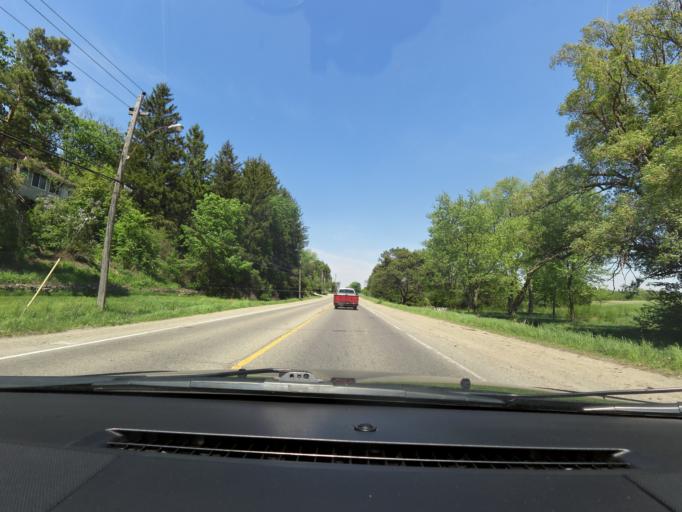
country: CA
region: Ontario
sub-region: Wellington County
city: Guelph
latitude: 43.5590
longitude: -80.2142
